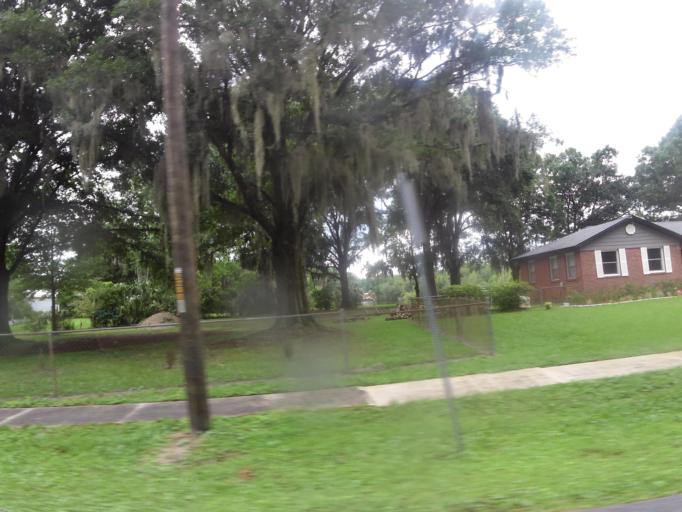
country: US
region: Florida
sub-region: Duval County
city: Jacksonville
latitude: 30.3042
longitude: -81.5532
